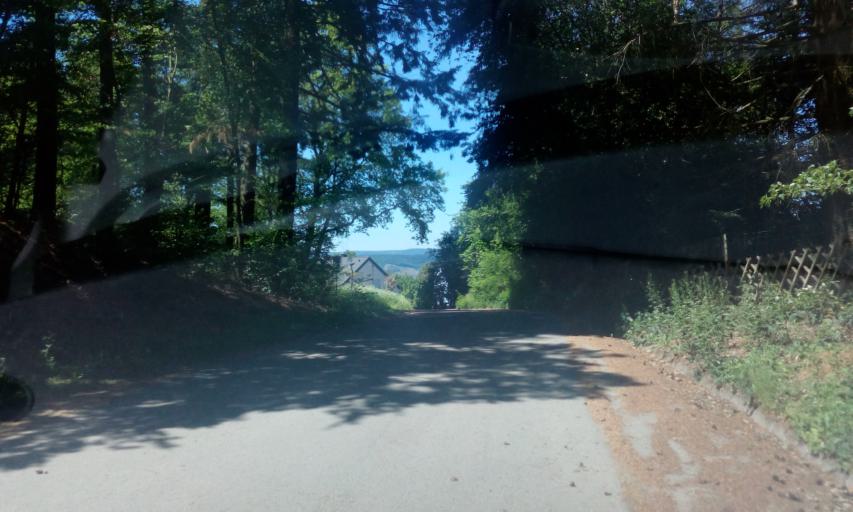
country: DE
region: Rheinland-Pfalz
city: Trittenheim
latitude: 49.8101
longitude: 6.9026
